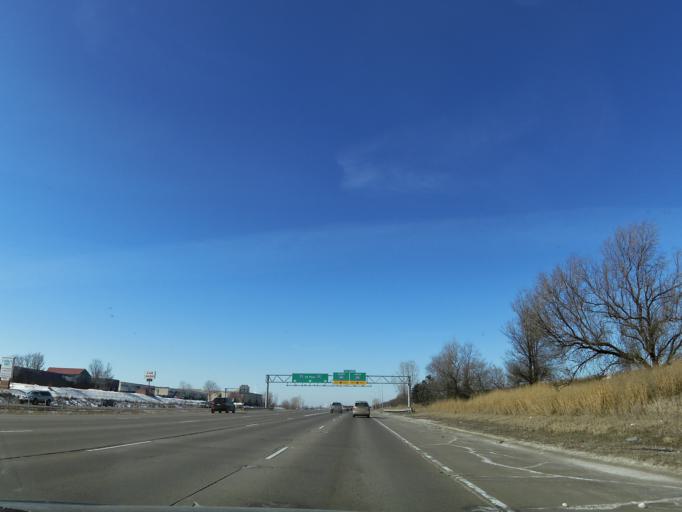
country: US
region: Minnesota
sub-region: Washington County
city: Oakdale
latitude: 44.9487
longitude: -92.9465
